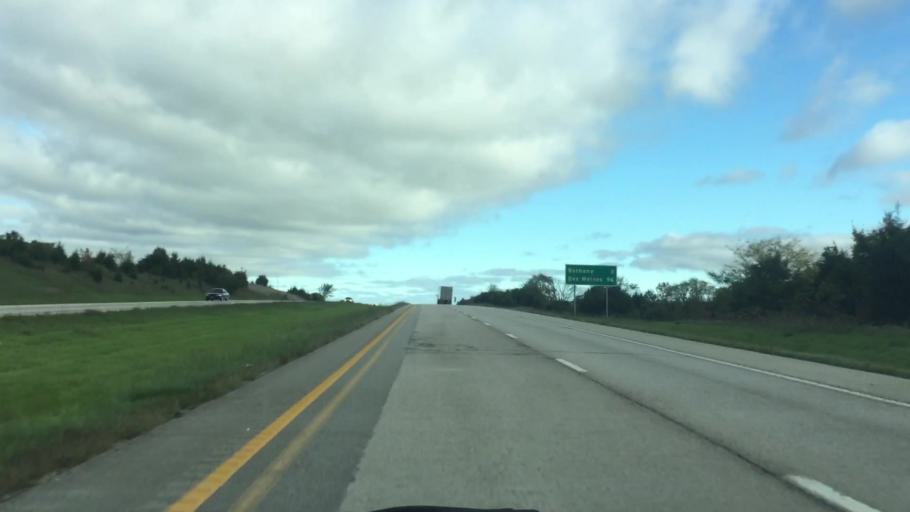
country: US
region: Missouri
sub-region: Harrison County
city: Bethany
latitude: 40.2221
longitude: -94.0129
